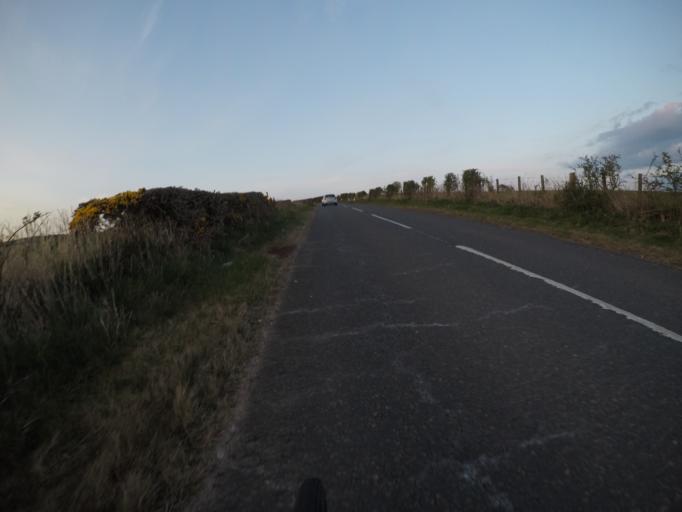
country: GB
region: Scotland
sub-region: South Ayrshire
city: Dundonald
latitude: 55.5574
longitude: -4.6136
